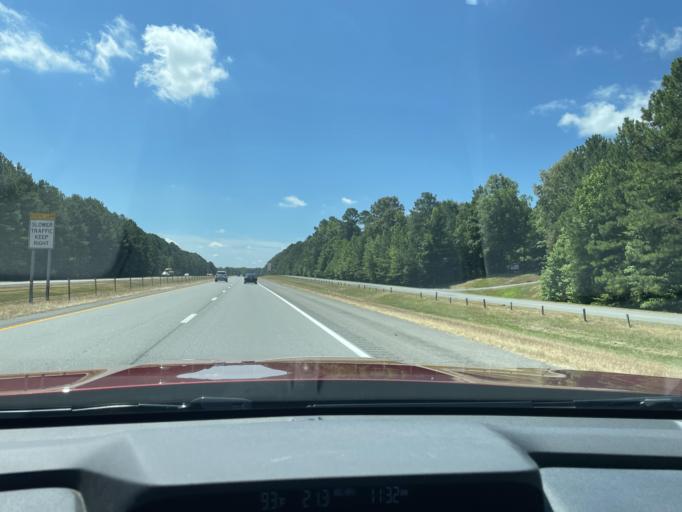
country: US
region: Arkansas
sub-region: Jefferson County
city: Redfield
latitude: 34.5018
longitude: -92.2153
